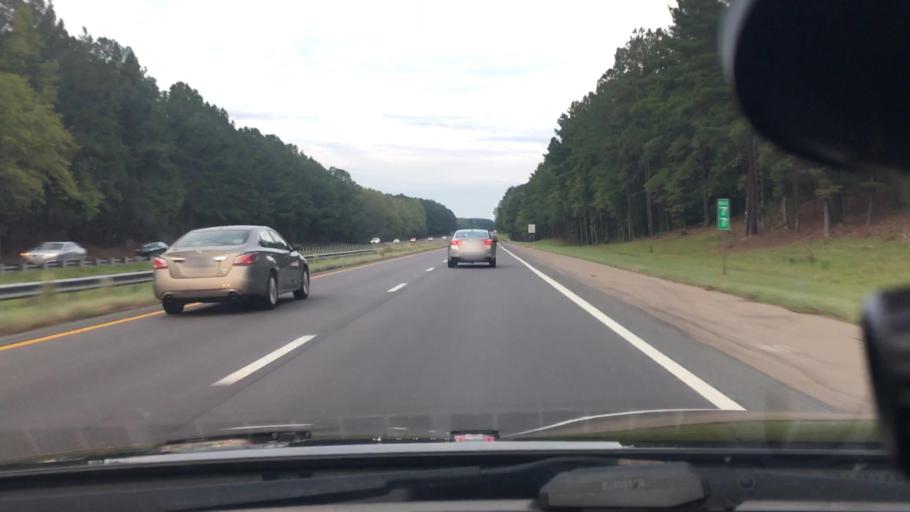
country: US
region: North Carolina
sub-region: Chatham County
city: Farmville
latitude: 35.5954
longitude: -79.1153
